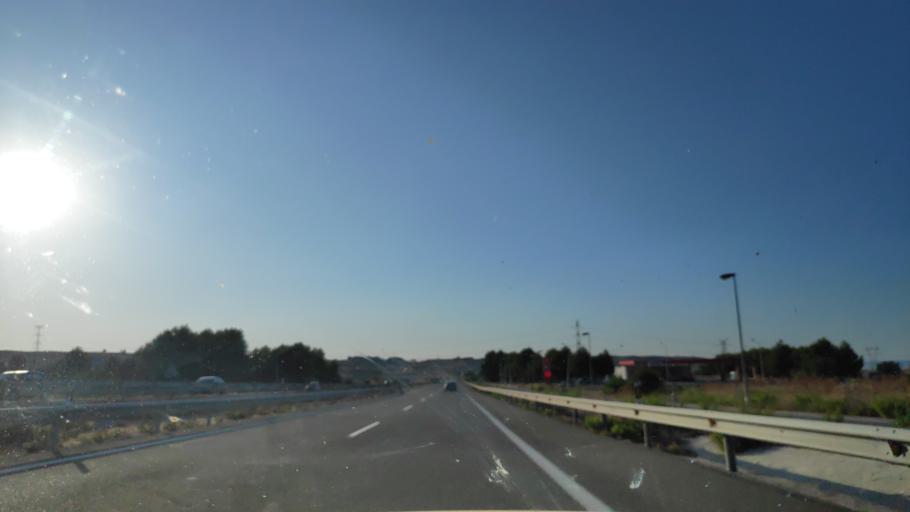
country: ES
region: Castille-La Mancha
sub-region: Provincia de Cuenca
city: Belinchon
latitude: 40.0312
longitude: -3.0399
